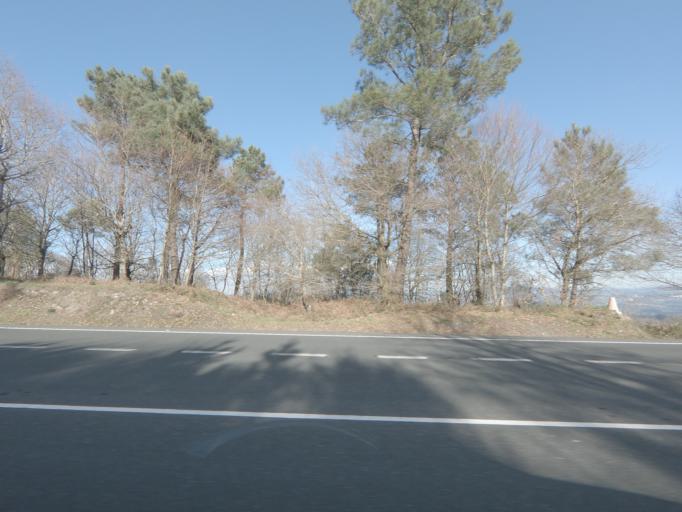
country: ES
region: Galicia
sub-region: Provincia de Pontevedra
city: Silleda
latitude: 42.7052
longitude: -8.3443
